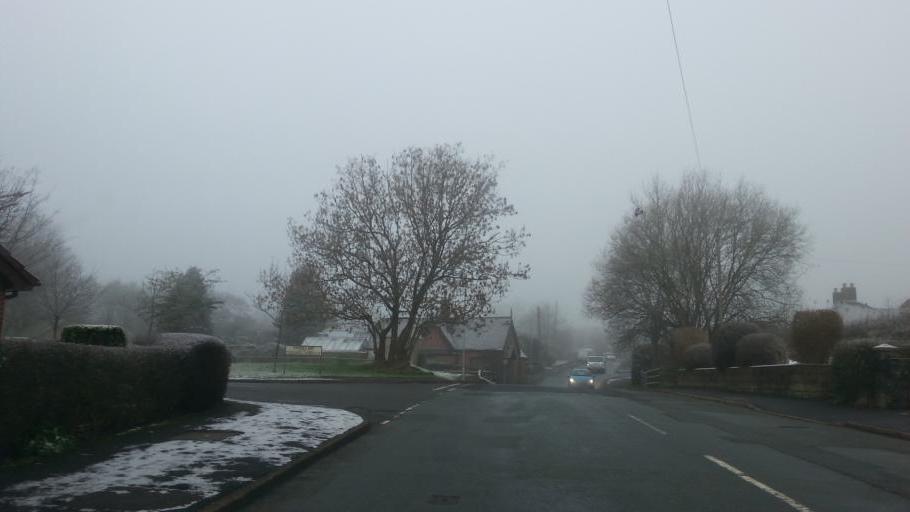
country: GB
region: England
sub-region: Staffordshire
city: Biddulph
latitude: 53.1222
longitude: -2.1780
